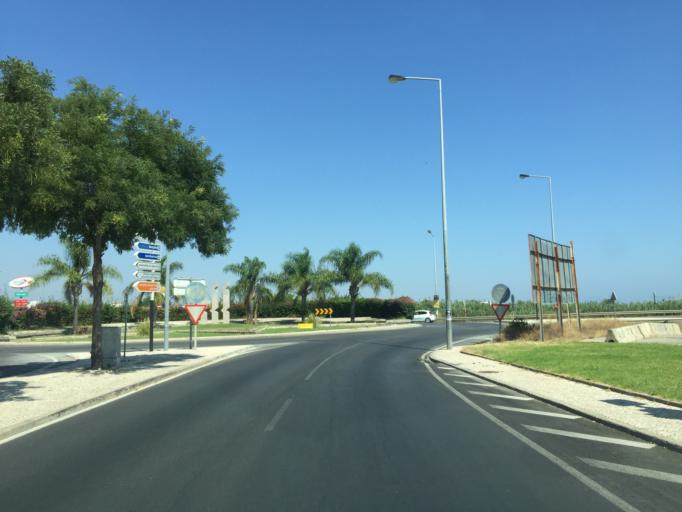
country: PT
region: Faro
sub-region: Faro
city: Faro
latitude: 37.0256
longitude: -7.9176
